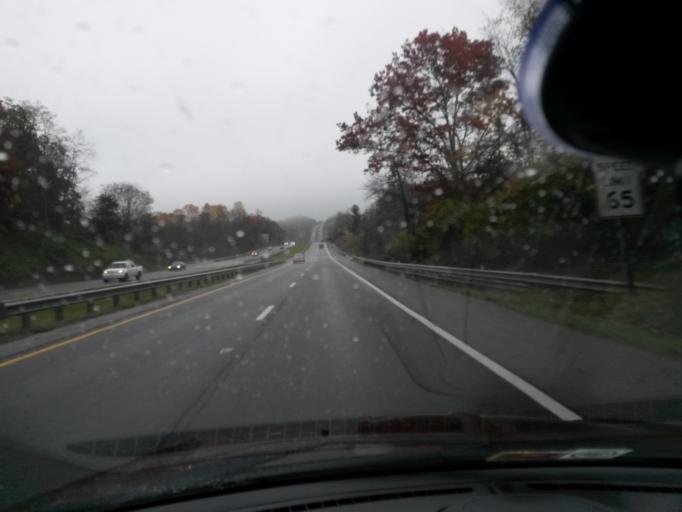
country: US
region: Virginia
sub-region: Montgomery County
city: Christiansburg
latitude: 37.1501
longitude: -80.3996
